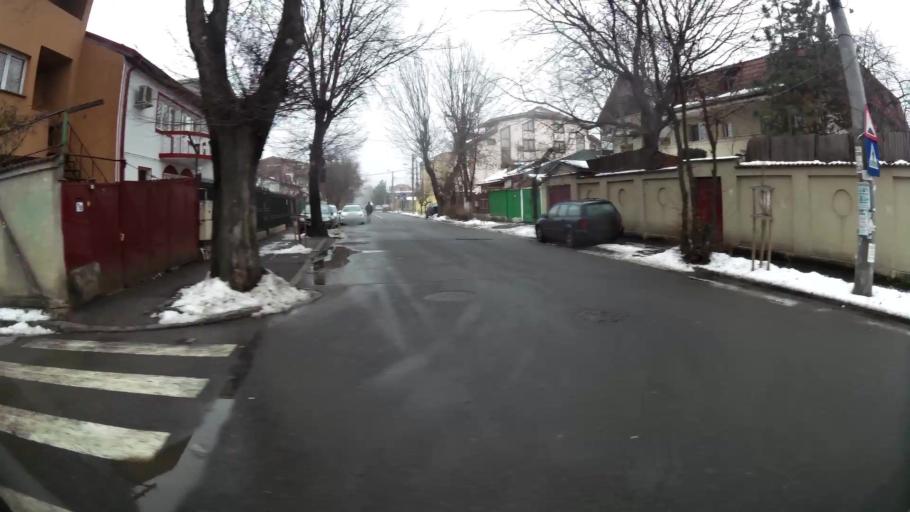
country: RO
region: Ilfov
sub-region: Comuna Chiajna
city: Rosu
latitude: 44.4437
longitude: 26.0271
